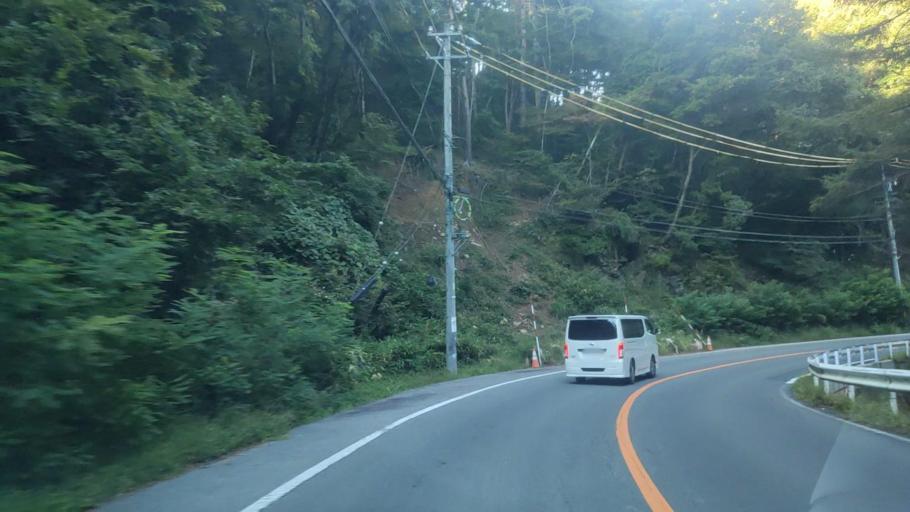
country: JP
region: Nagano
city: Kamimaruko
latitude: 36.2438
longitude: 138.3074
